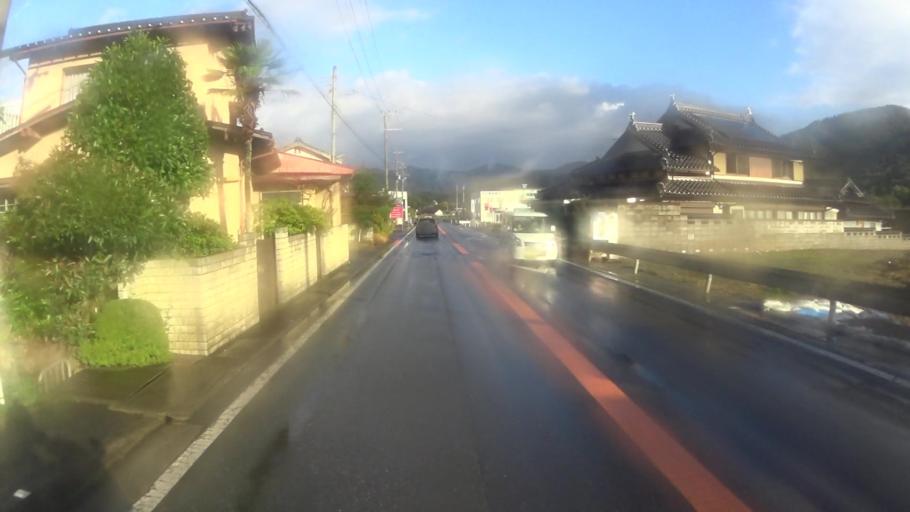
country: JP
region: Kyoto
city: Ayabe
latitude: 35.2405
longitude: 135.2180
